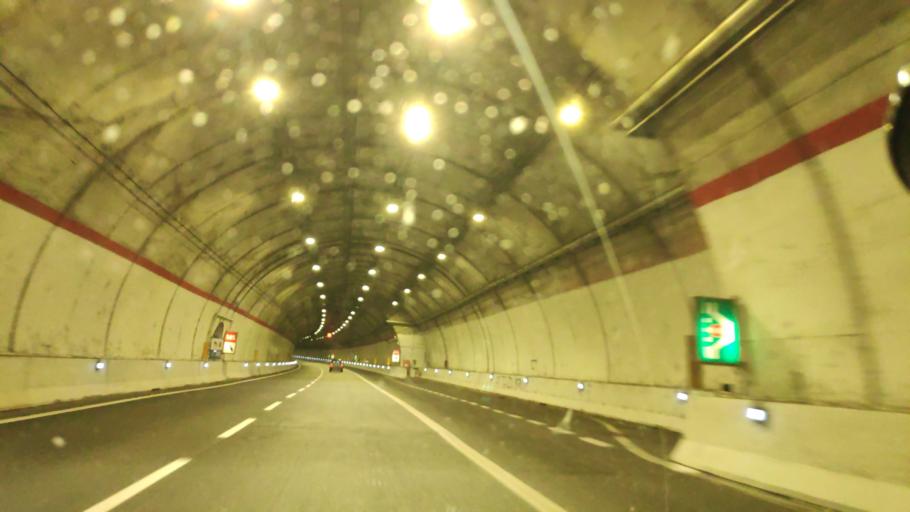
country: IT
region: Campania
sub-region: Provincia di Salerno
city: Sicignano degli Alburni
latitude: 40.6034
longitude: 15.3021
